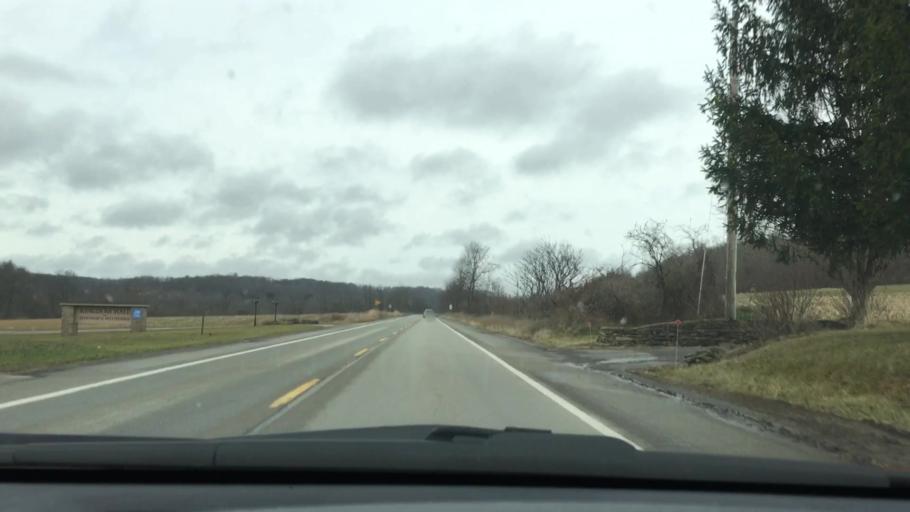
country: US
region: Pennsylvania
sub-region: Greene County
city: Fairdale
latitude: 39.8619
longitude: -79.9646
